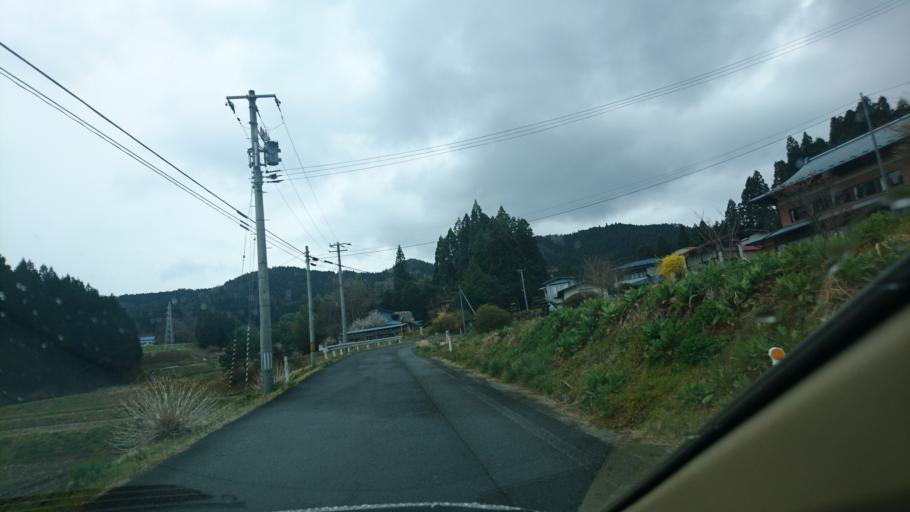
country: JP
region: Iwate
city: Ichinoseki
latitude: 38.9436
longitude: 141.3075
